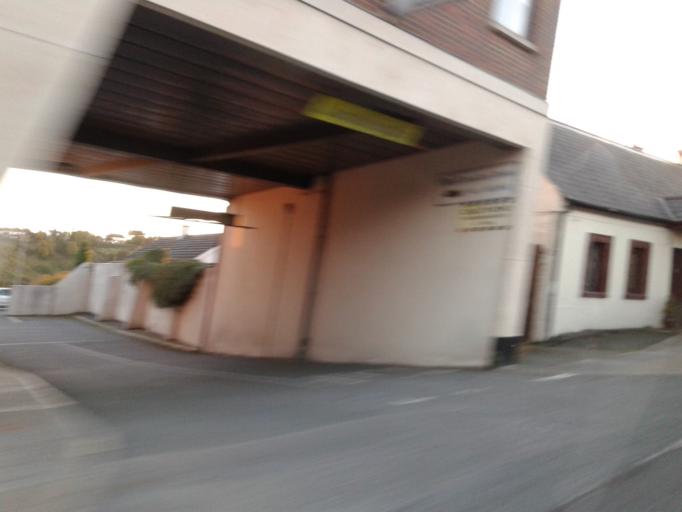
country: IE
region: Leinster
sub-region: Lu
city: Drogheda
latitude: 53.7192
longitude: -6.3734
